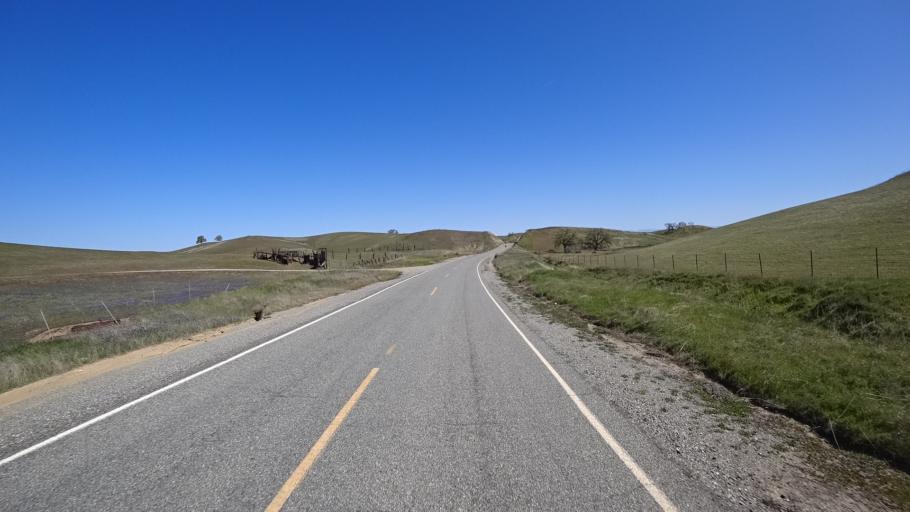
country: US
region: California
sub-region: Tehama County
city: Rancho Tehama Reserve
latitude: 39.8224
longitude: -122.3802
